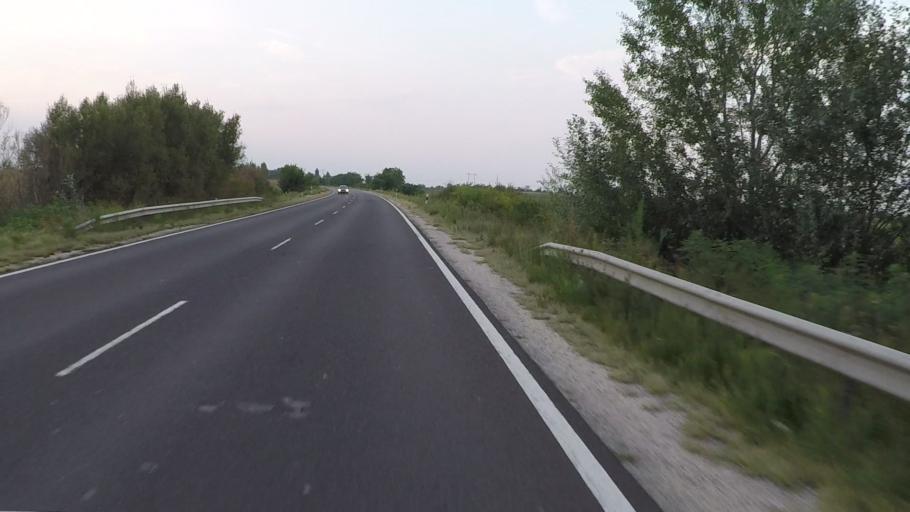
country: HU
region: Pest
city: Abony
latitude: 47.2042
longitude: 20.0741
